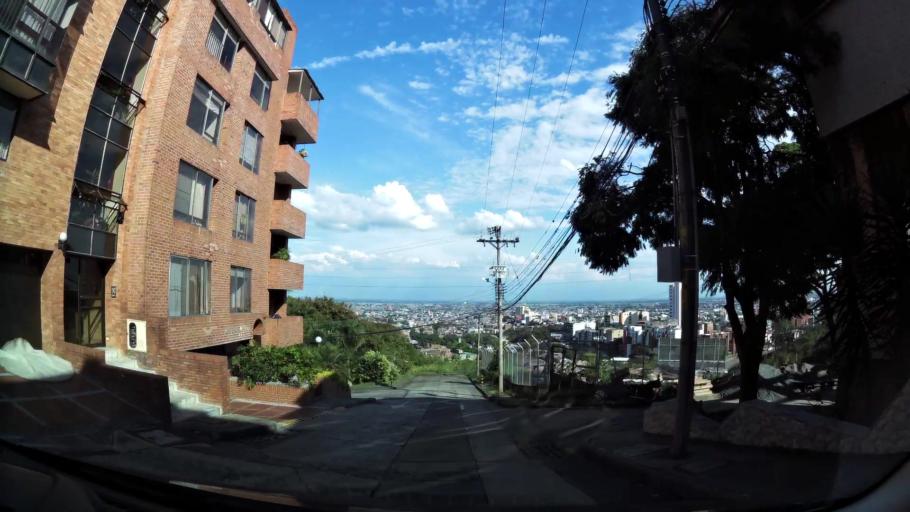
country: CO
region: Valle del Cauca
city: Cali
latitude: 3.4453
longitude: -76.5494
